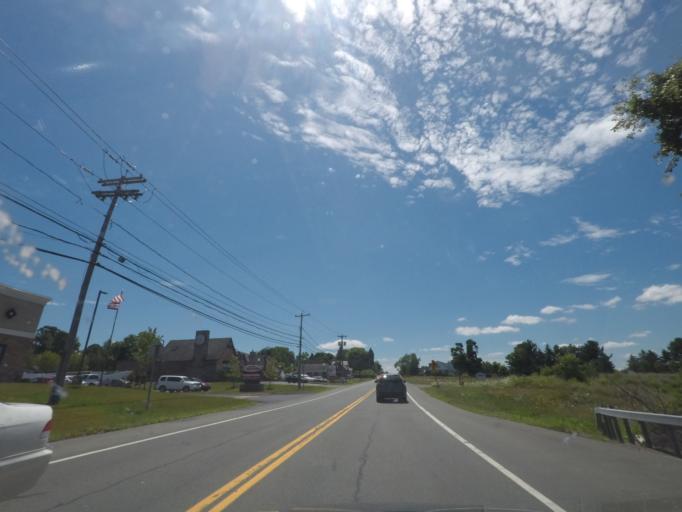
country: US
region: New York
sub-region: Albany County
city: Menands
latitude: 42.6909
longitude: -73.6871
